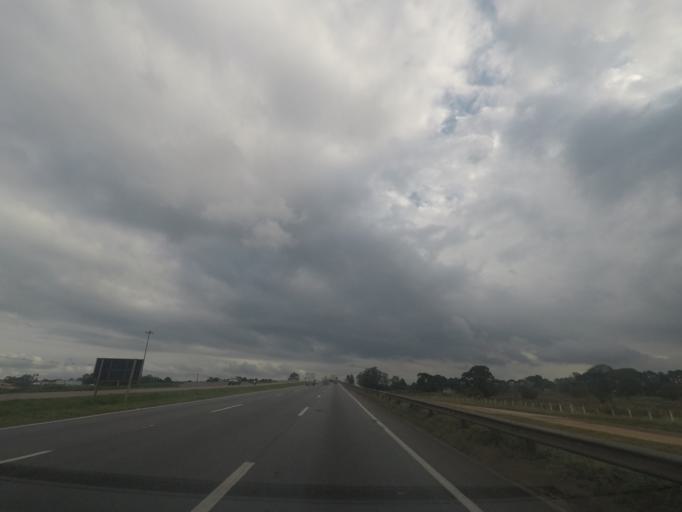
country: BR
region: Parana
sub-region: Sao Jose Dos Pinhais
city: Sao Jose dos Pinhais
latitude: -25.5303
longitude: -49.1435
